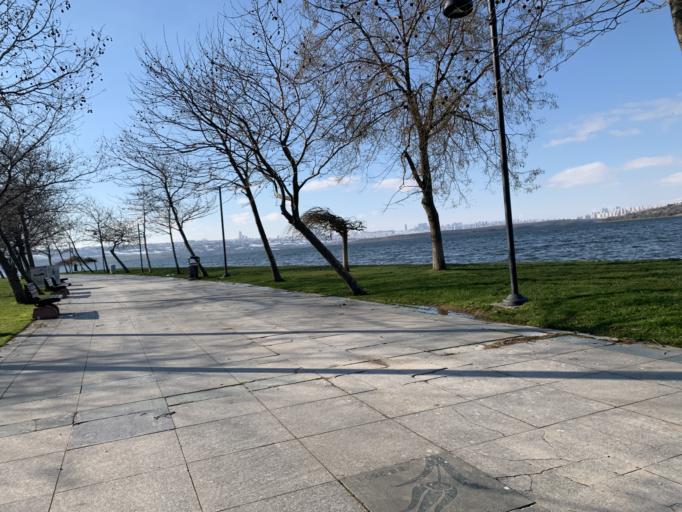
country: TR
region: Istanbul
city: Mahmutbey
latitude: 41.0002
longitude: 28.7650
